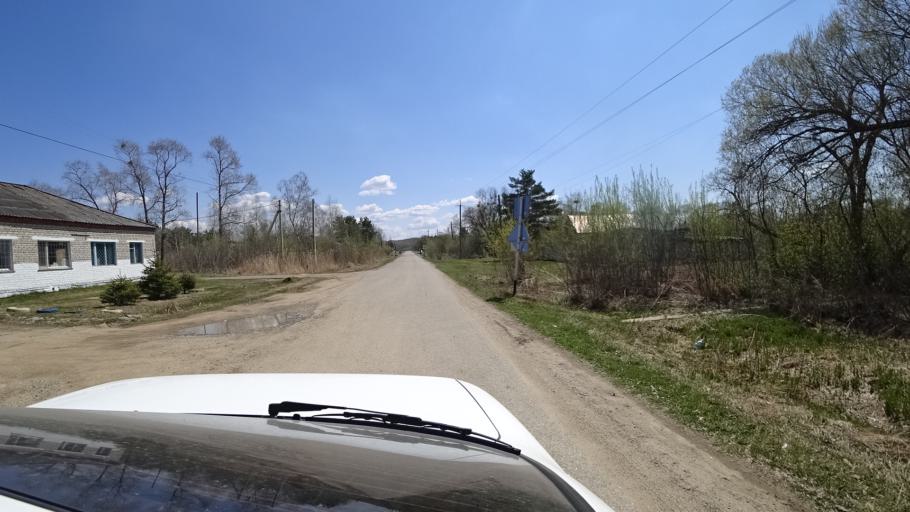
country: RU
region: Primorskiy
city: Lazo
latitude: 45.7956
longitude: 133.7654
